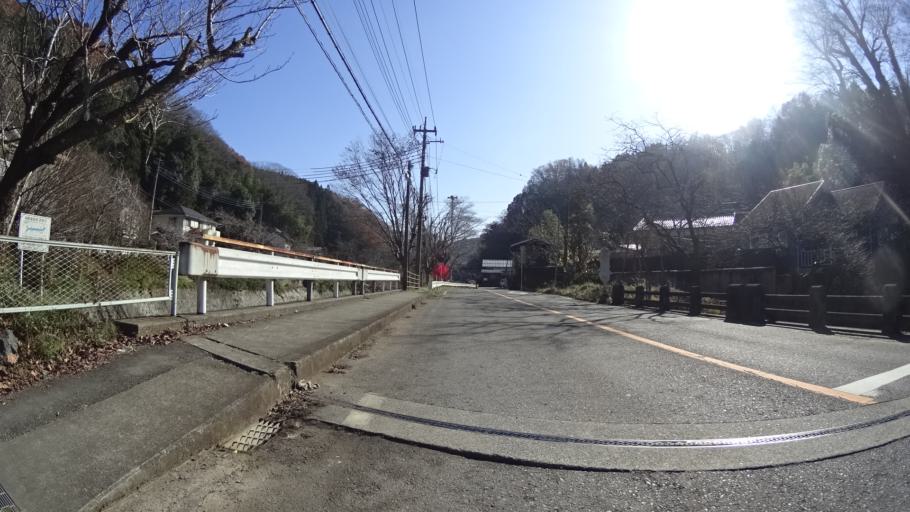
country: JP
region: Yamanashi
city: Uenohara
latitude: 35.6265
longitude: 139.1491
